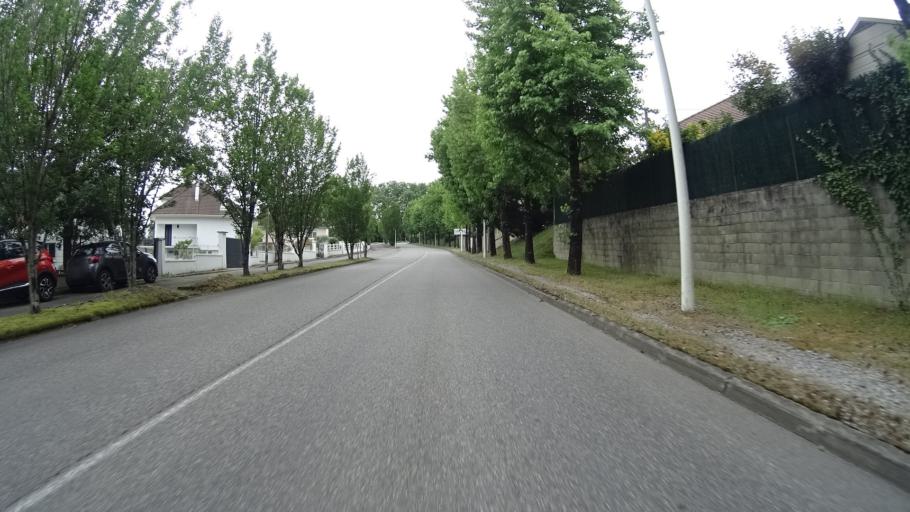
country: FR
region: Aquitaine
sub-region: Departement des Pyrenees-Atlantiques
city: Orthez
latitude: 43.4916
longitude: -0.7627
